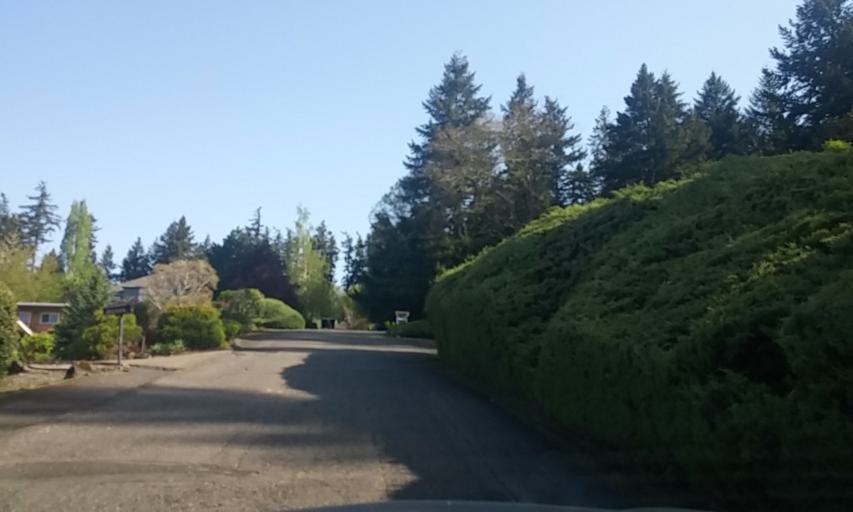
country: US
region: Oregon
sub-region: Washington County
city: Metzger
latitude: 45.4345
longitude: -122.7341
